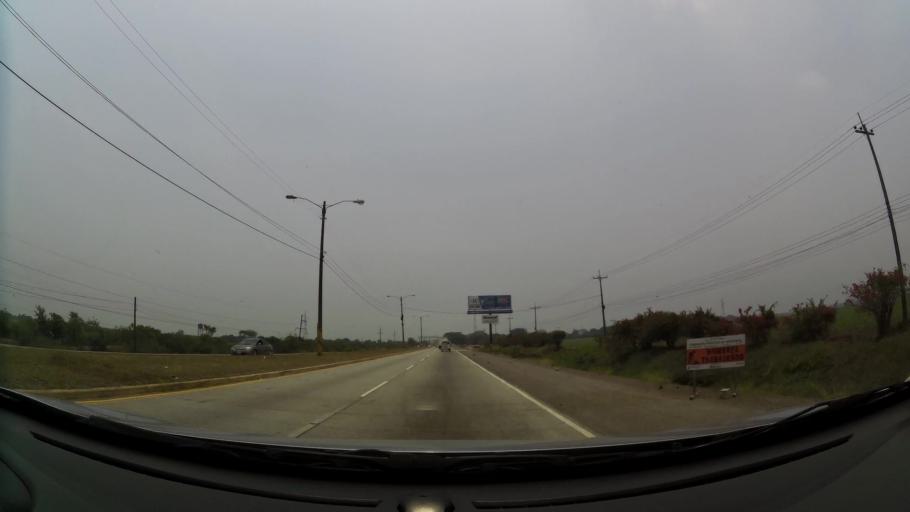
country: HN
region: Yoro
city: El Progreso
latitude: 15.4118
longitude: -87.8571
